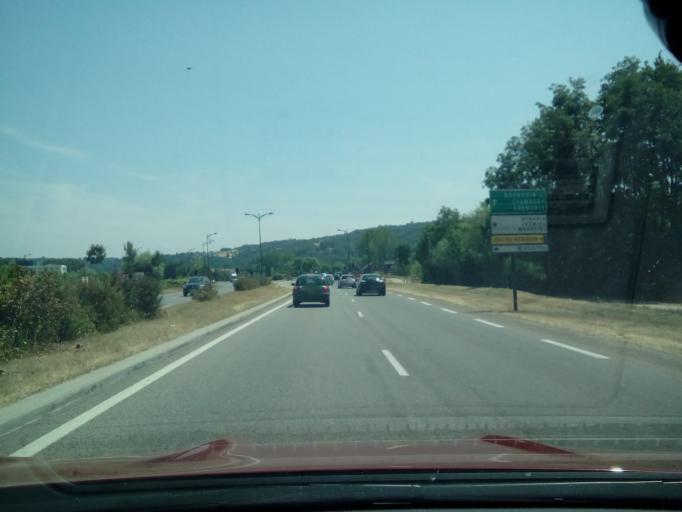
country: FR
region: Rhone-Alpes
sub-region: Departement de l'Isere
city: Domarin
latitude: 45.5976
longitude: 5.2395
